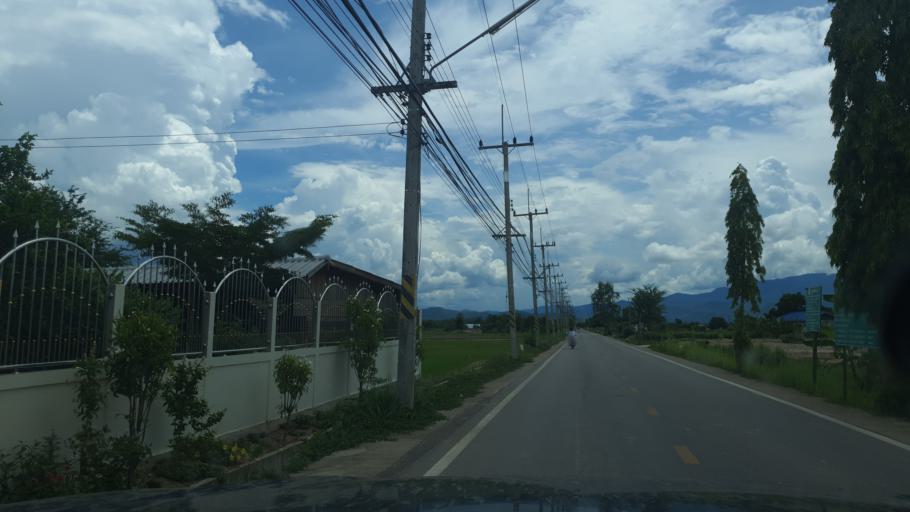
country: TH
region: Lampang
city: Sop Prap
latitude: 17.8840
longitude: 99.3797
